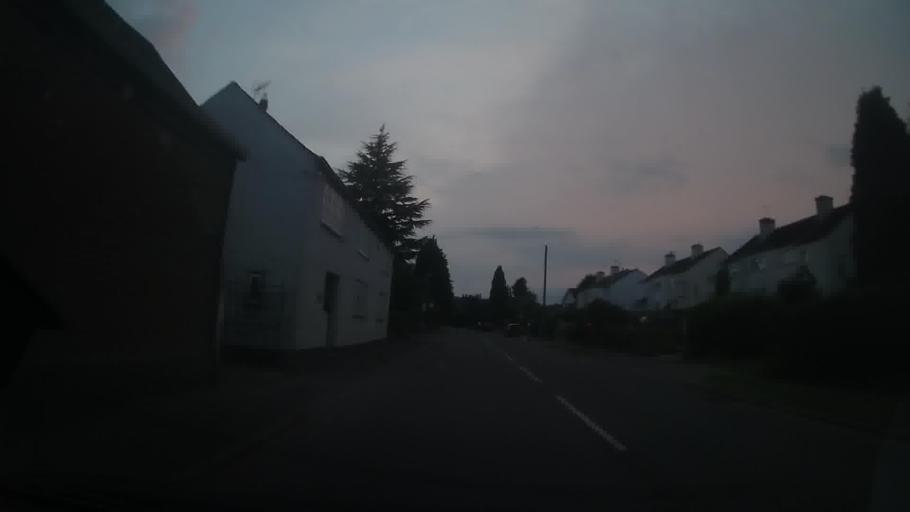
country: GB
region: England
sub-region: Leicestershire
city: Quorndon
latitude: 52.7135
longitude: -1.1919
